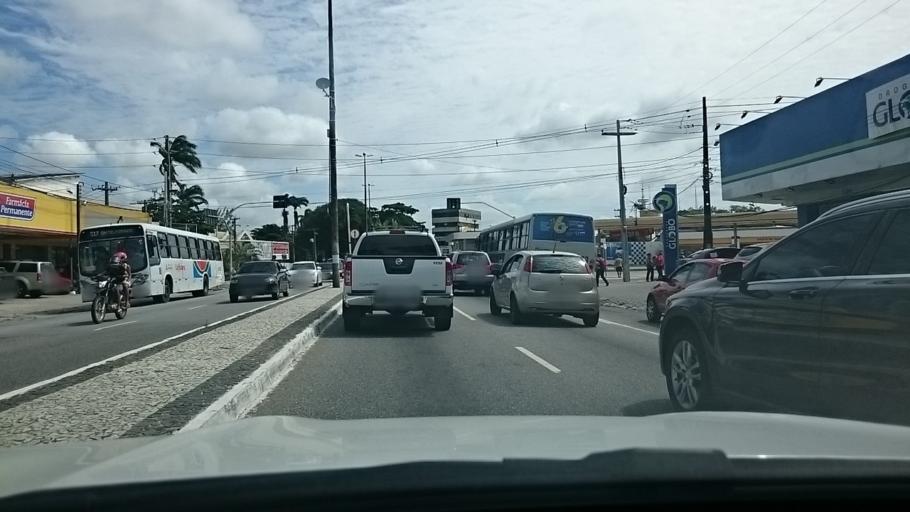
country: BR
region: Paraiba
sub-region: Joao Pessoa
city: Joao Pessoa
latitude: -7.1198
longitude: -34.8666
